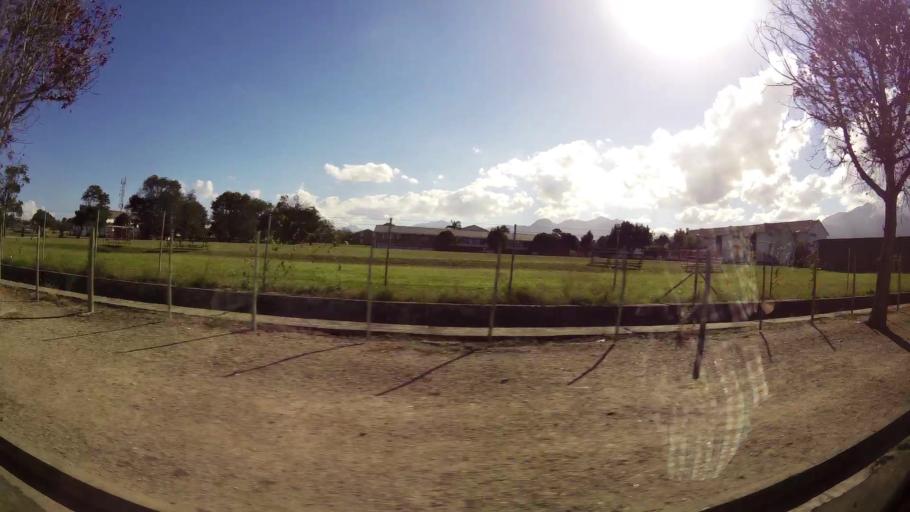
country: ZA
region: Western Cape
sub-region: Eden District Municipality
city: George
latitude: -33.9752
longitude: 22.4482
